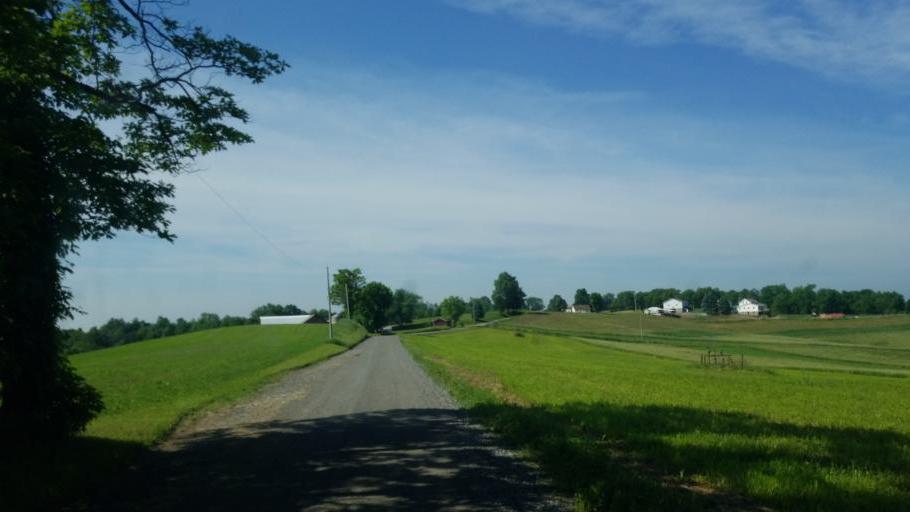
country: US
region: Ohio
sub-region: Tuscarawas County
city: Sugarcreek
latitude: 40.4576
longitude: -81.7639
